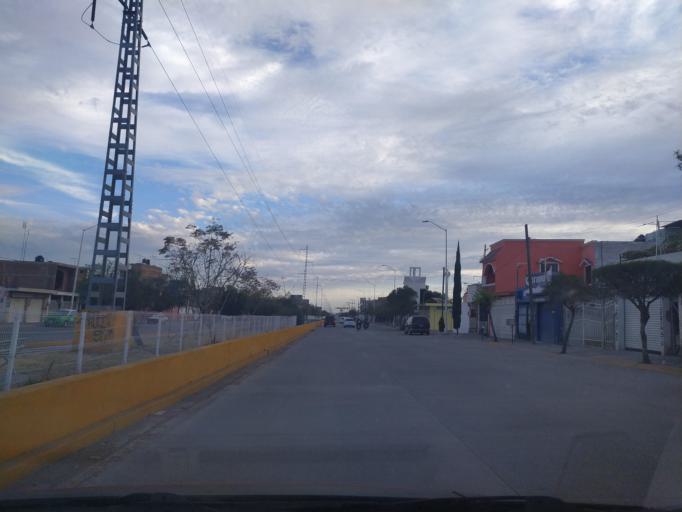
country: LA
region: Oudomxai
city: Muang La
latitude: 21.0269
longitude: 101.8695
